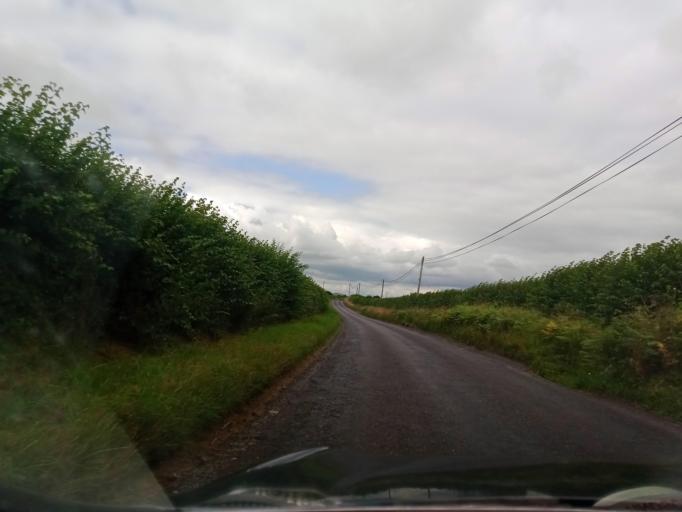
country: IE
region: Leinster
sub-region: Laois
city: Stradbally
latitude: 52.9871
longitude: -7.1811
